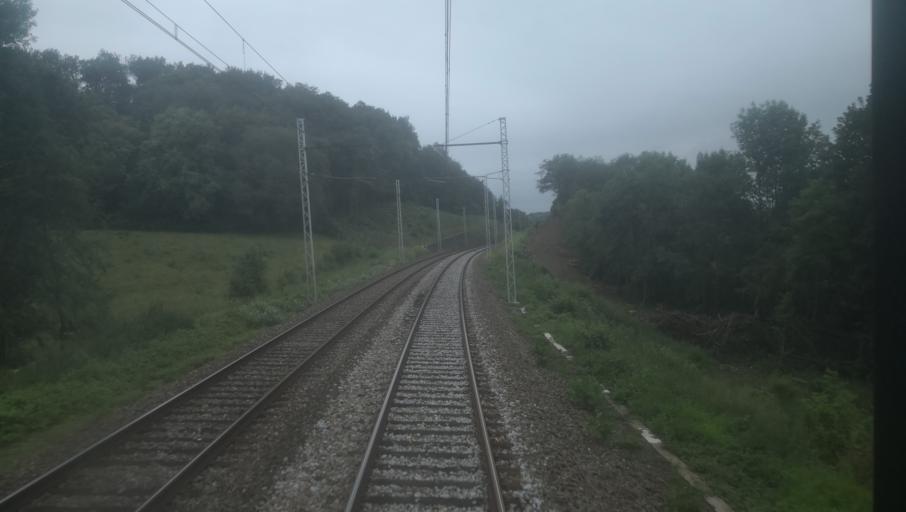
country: FR
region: Centre
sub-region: Departement de l'Indre
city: Le Pechereau
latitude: 46.5608
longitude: 1.5272
